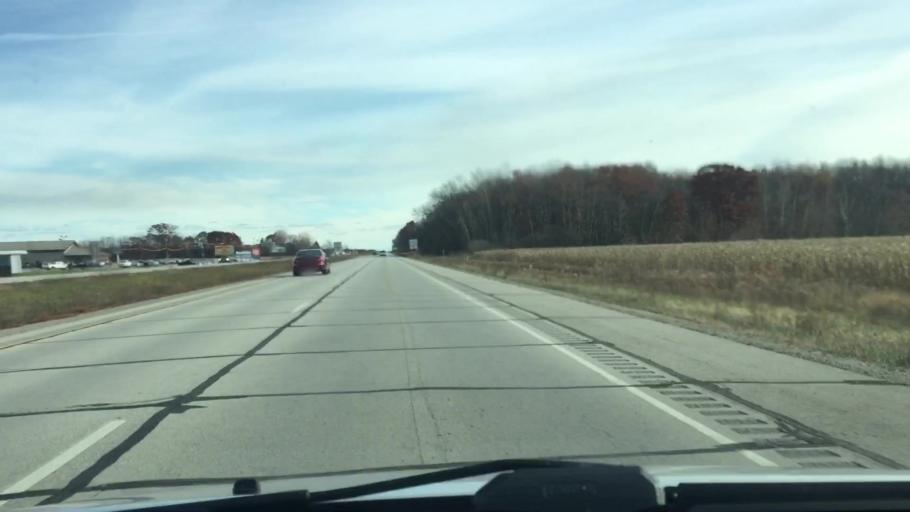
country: US
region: Wisconsin
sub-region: Brown County
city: Oneida
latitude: 44.5736
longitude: -88.1641
